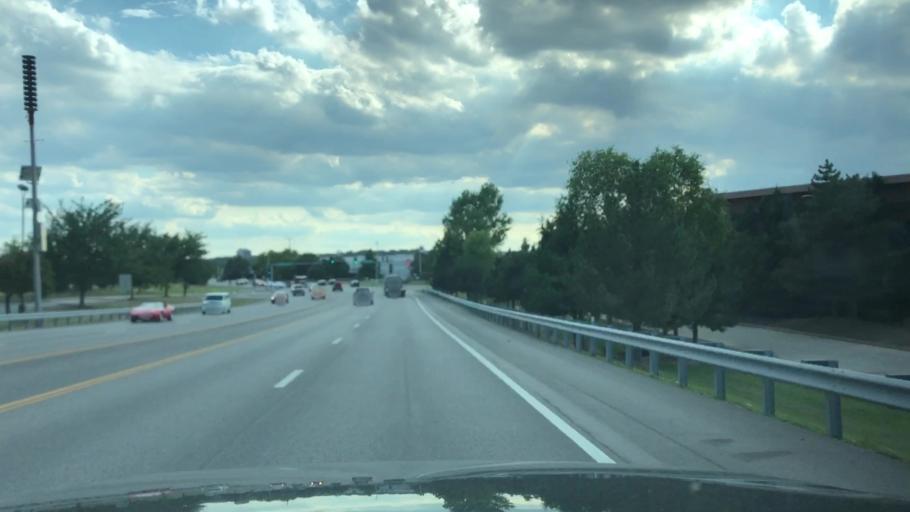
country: US
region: Missouri
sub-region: Saint Charles County
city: Saint Charles
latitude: 38.7888
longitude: -90.4562
